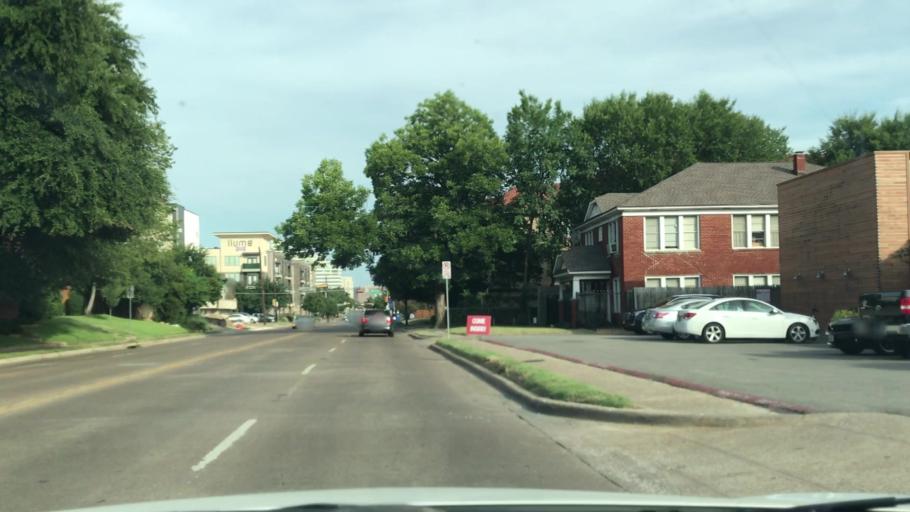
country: US
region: Texas
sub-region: Dallas County
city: Highland Park
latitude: 32.8148
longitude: -96.8160
